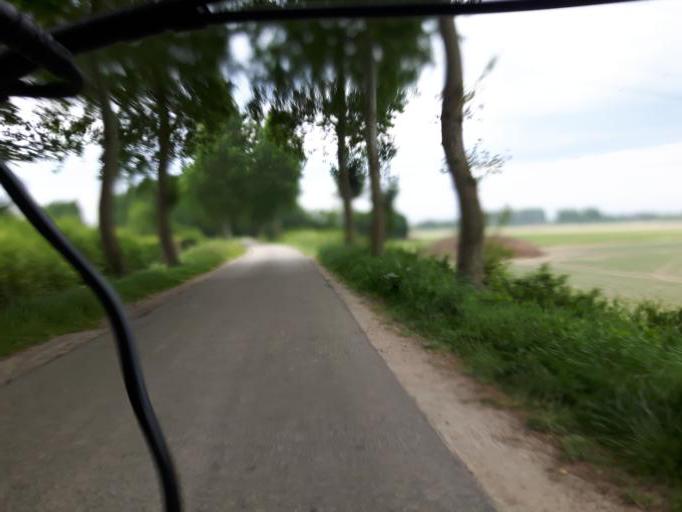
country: NL
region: Zeeland
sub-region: Gemeente Borsele
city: Borssele
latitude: 51.4333
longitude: 3.7954
